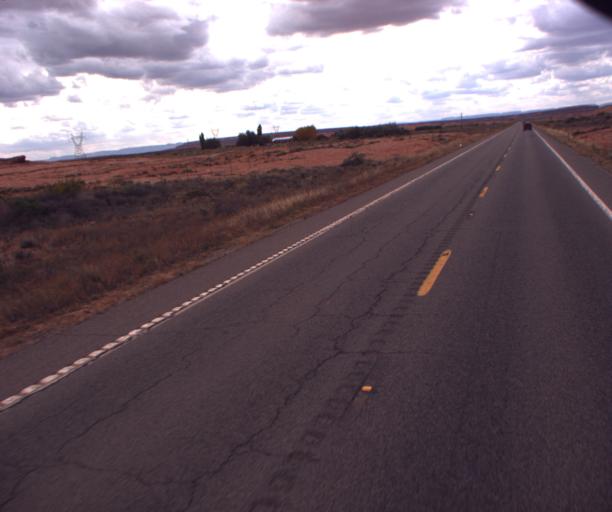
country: US
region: Arizona
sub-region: Navajo County
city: Kayenta
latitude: 36.8318
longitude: -109.8568
